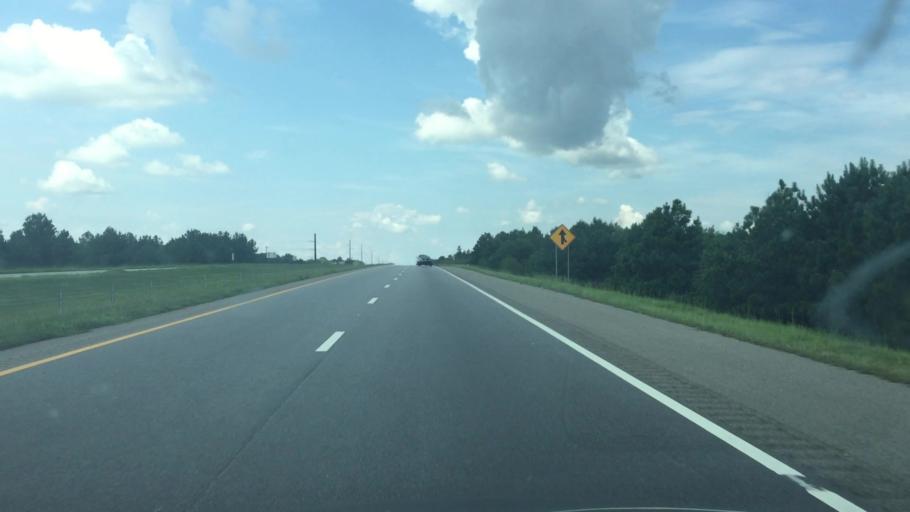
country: US
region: North Carolina
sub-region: Richmond County
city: Hamlet
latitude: 34.8652
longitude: -79.6685
